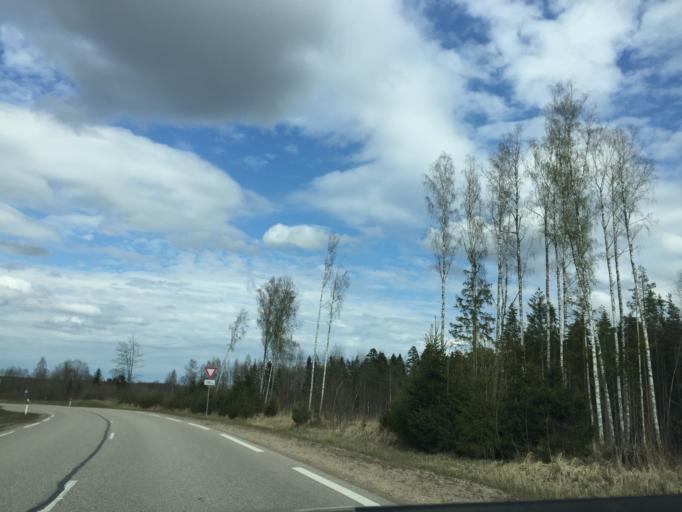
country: LV
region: Jaunpiebalga
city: Jaunpiebalga
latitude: 57.2369
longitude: 26.2525
